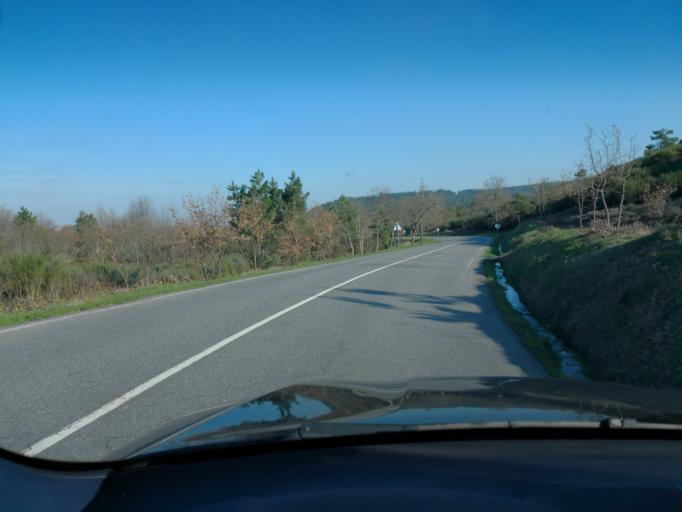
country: PT
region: Vila Real
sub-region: Sabrosa
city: Sabrosa
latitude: 41.3607
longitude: -7.6352
